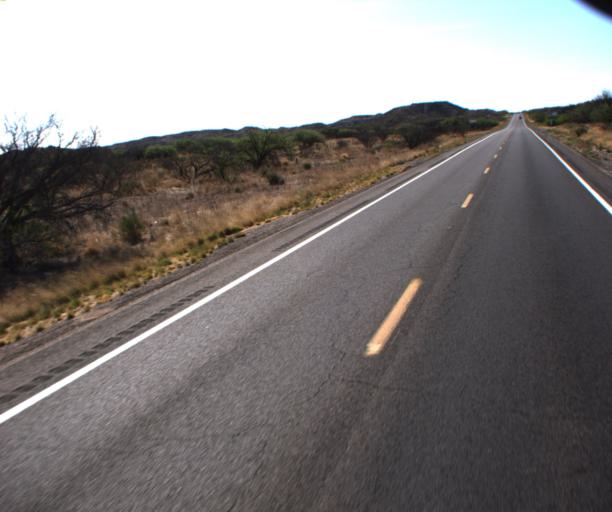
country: US
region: Arizona
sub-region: Cochise County
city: Saint David
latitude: 31.8354
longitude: -110.1851
